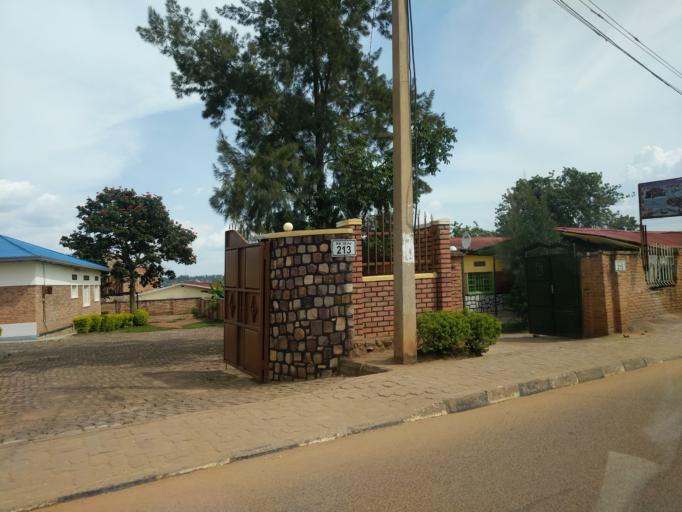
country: RW
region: Kigali
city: Kigali
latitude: -1.9809
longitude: 30.1332
